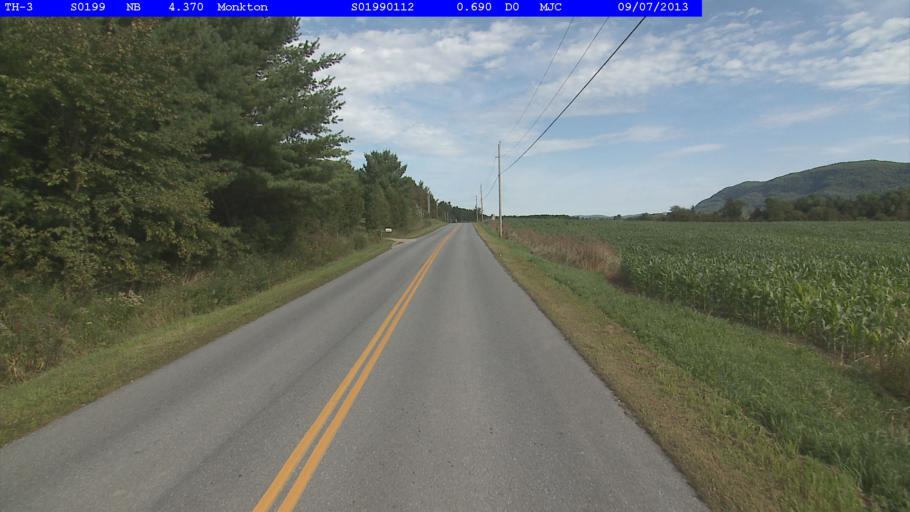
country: US
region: Vermont
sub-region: Addison County
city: Bristol
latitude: 44.1905
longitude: -73.1085
